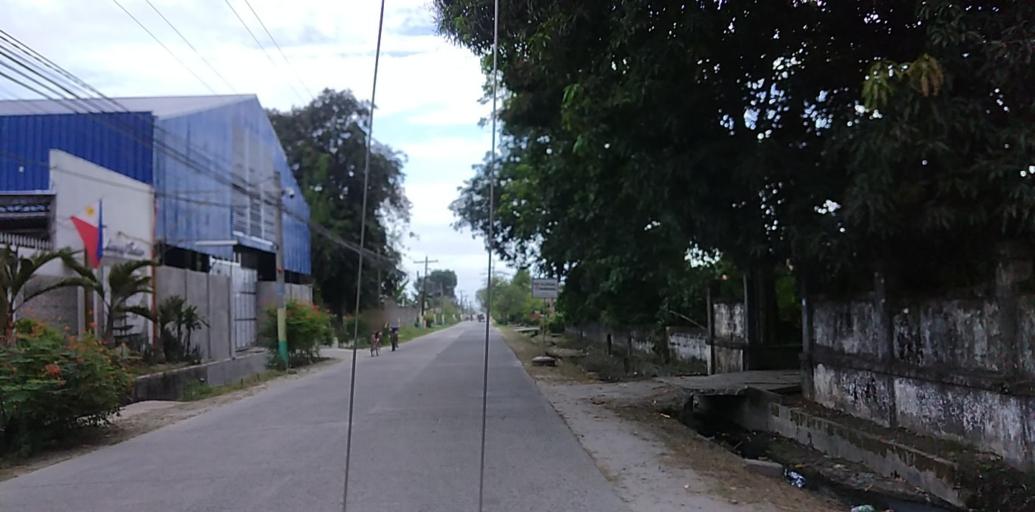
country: PH
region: Central Luzon
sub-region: Province of Pampanga
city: Pulung Santol
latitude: 15.0427
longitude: 120.5614
